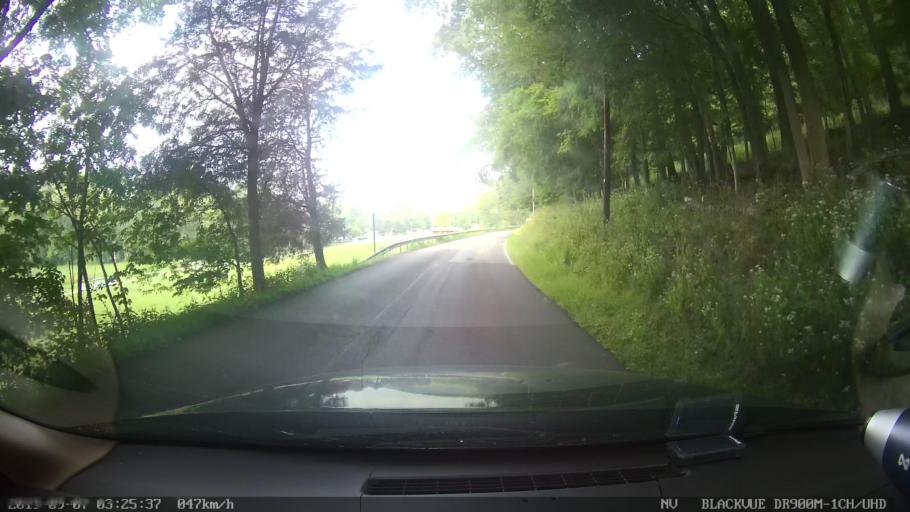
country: US
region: Ohio
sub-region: Licking County
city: Granville
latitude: 40.1224
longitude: -82.4877
